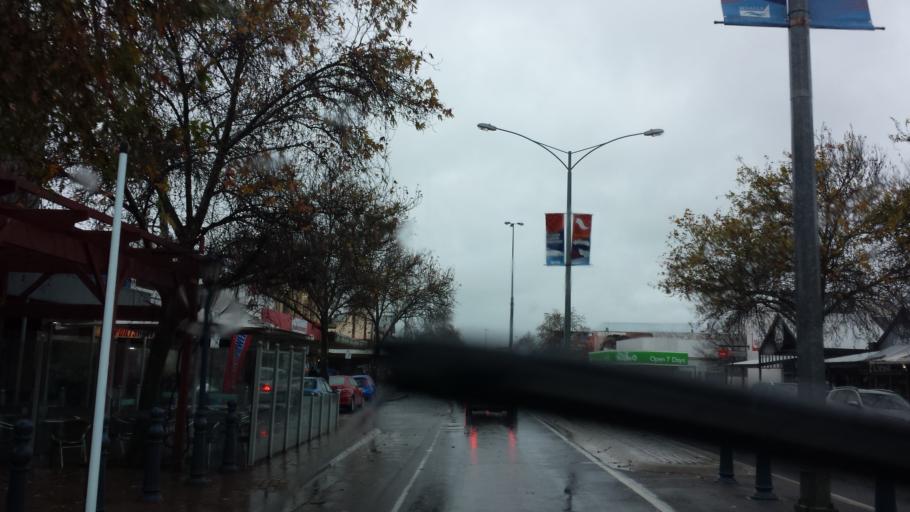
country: AU
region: Victoria
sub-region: Benalla
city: Benalla
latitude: -36.5514
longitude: 145.9849
